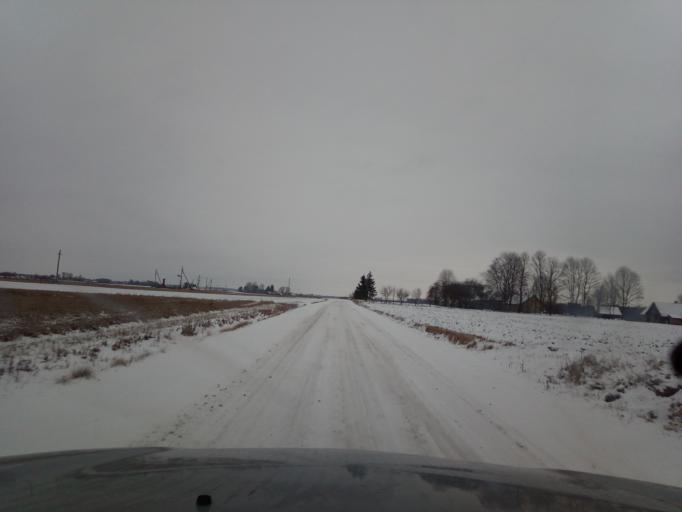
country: LT
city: Ramygala
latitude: 55.4955
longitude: 24.5359
